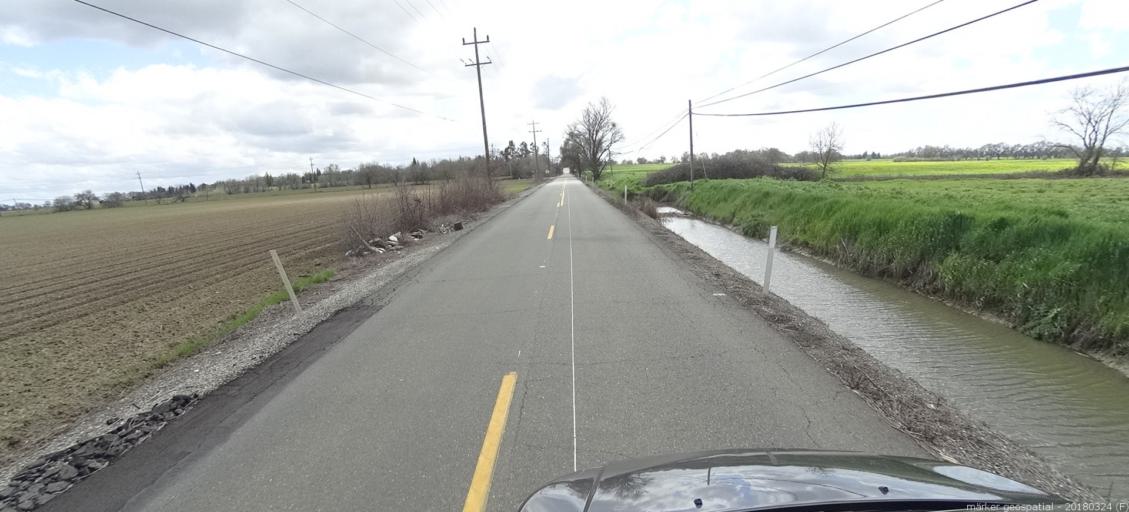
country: US
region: California
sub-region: Yolo County
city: West Sacramento
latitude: 38.6583
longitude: -121.5767
